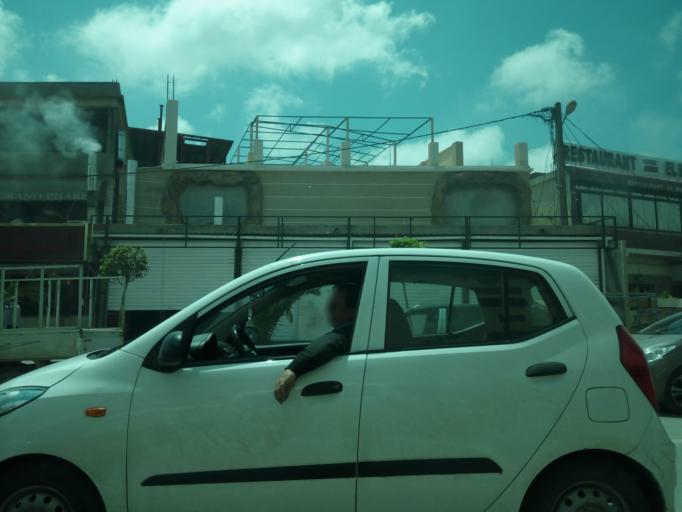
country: DZ
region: Tipaza
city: Saoula
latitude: 36.7231
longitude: 2.9915
